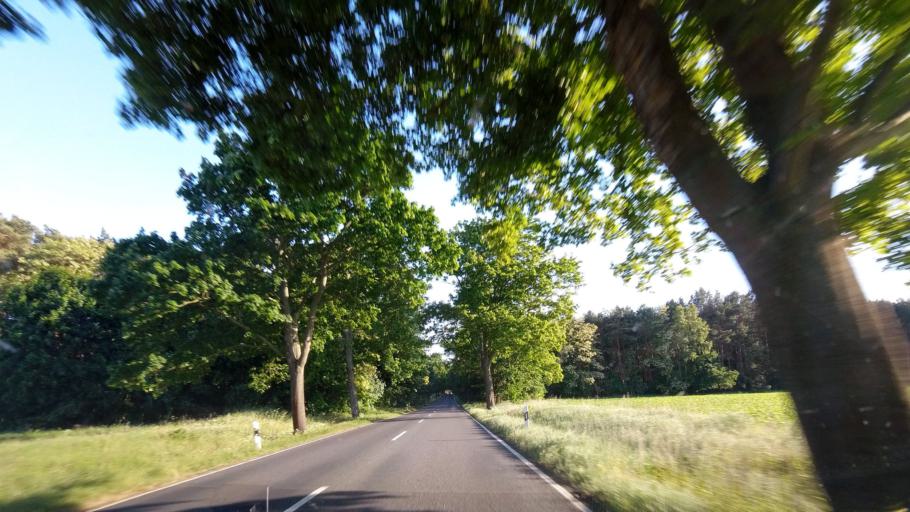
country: DE
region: Brandenburg
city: Golzow
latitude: 52.3050
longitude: 12.6066
